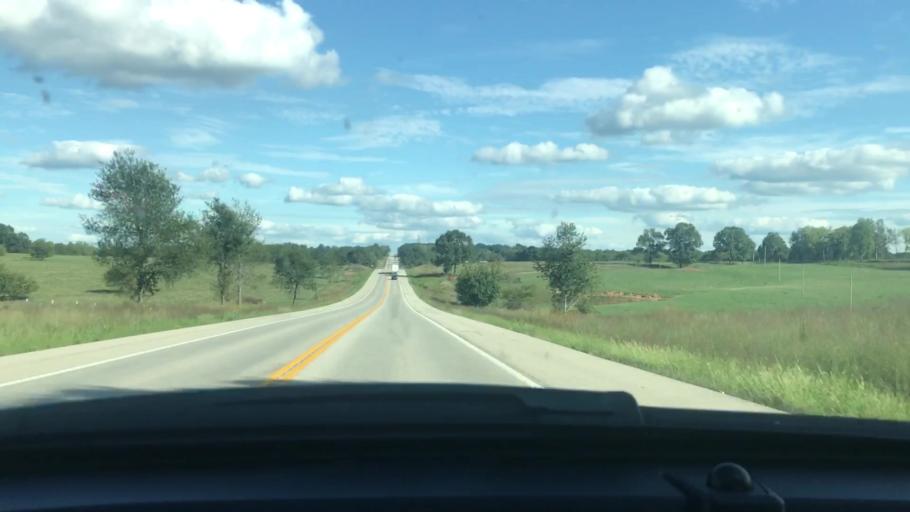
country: US
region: Missouri
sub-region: Howell County
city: West Plains
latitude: 36.6583
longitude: -91.7039
